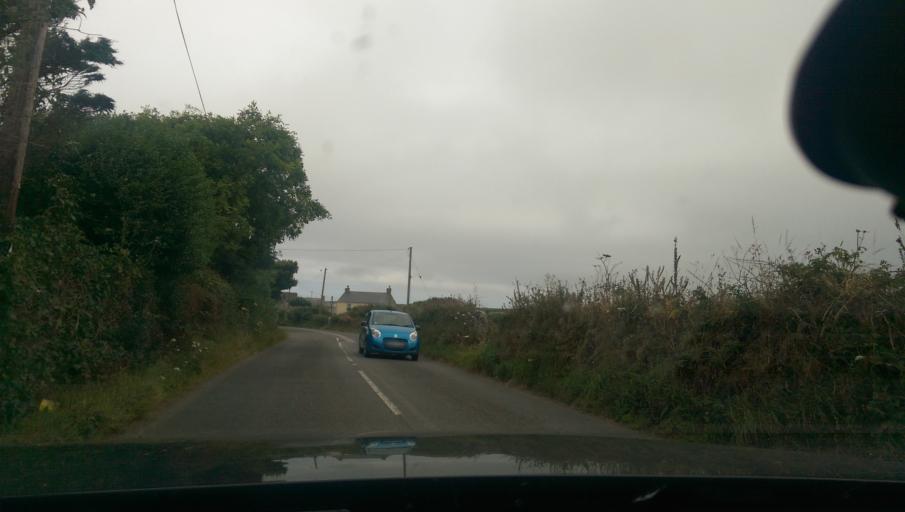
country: GB
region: England
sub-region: Cornwall
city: Saint Just
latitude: 50.1102
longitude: -5.6764
